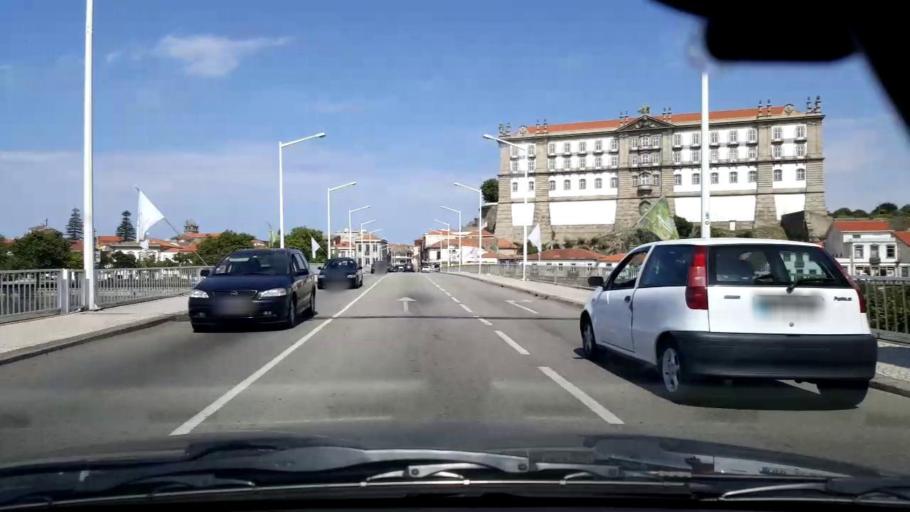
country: PT
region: Porto
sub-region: Vila do Conde
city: Vila do Conde
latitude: 41.3506
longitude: -8.7391
